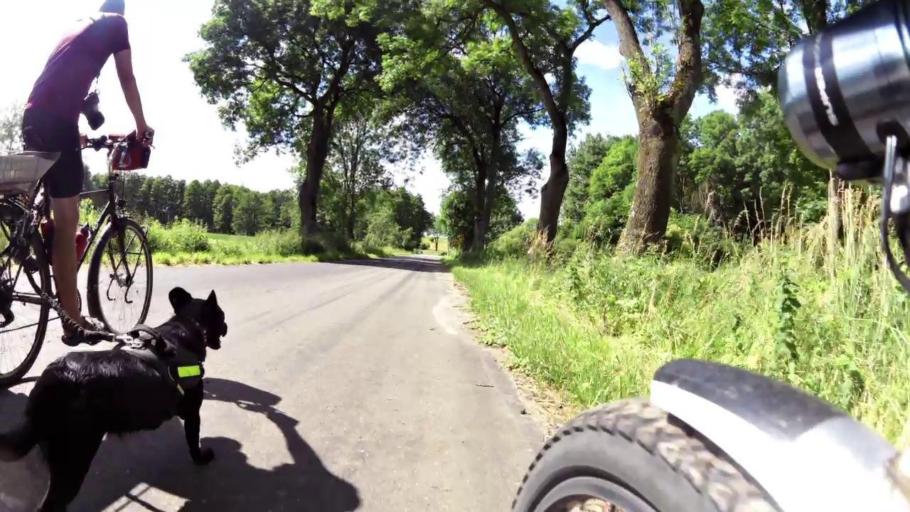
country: PL
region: West Pomeranian Voivodeship
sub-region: Powiat lobeski
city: Radowo Male
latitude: 53.5677
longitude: 15.4128
